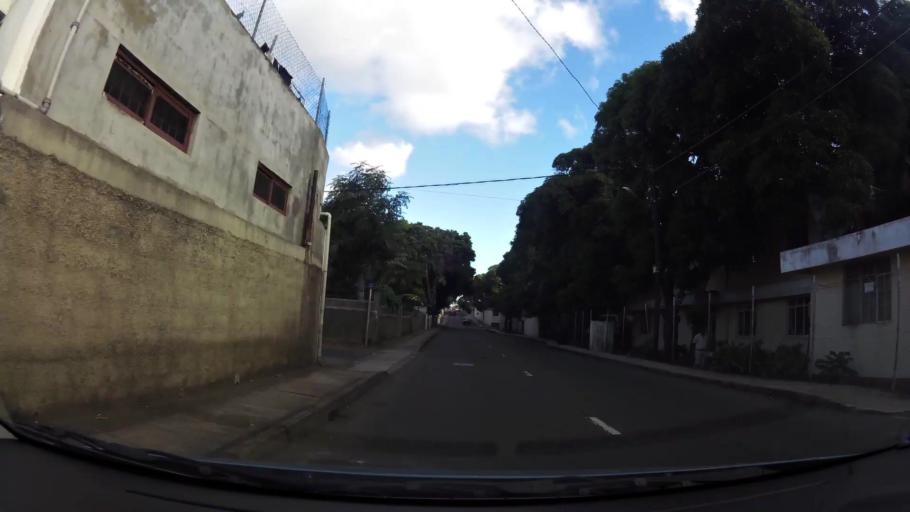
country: MU
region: Plaines Wilhems
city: Ebene
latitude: -20.2281
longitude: 57.4634
